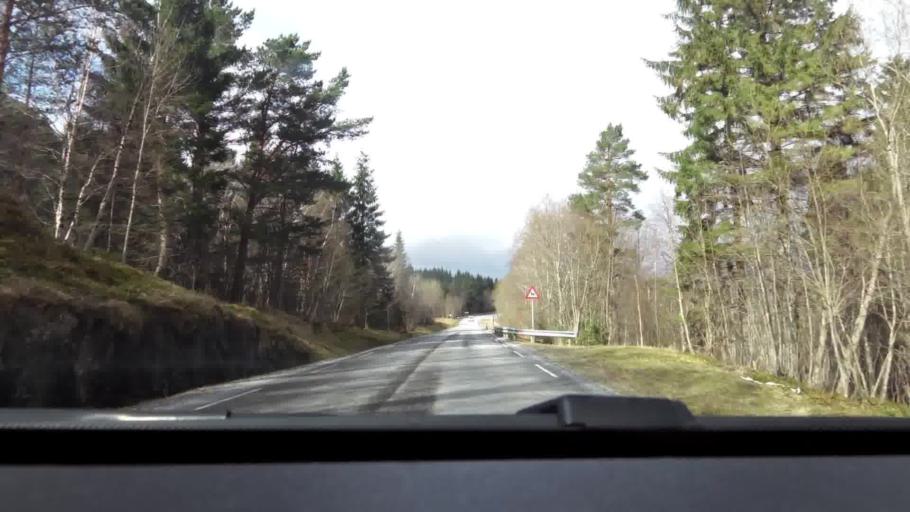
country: NO
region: More og Romsdal
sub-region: Averoy
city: Bruhagen
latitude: 63.1026
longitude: 7.6271
